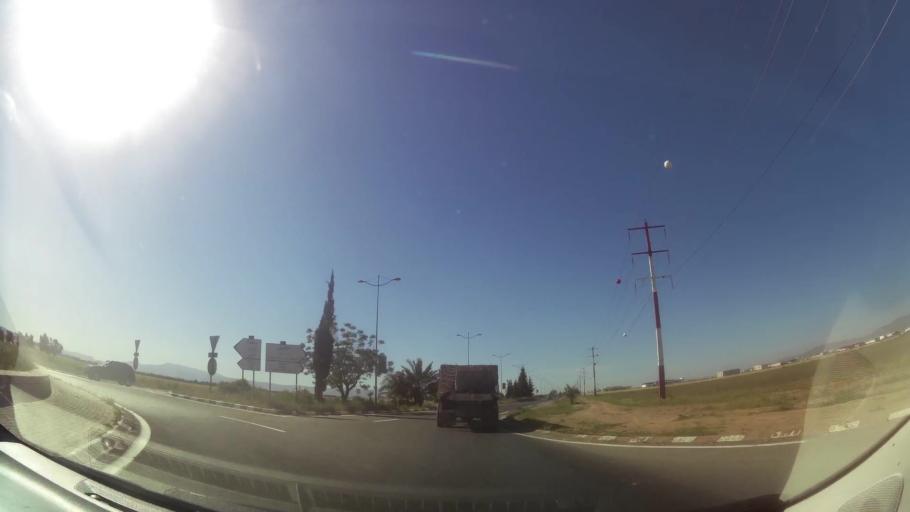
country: MA
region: Oriental
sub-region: Oujda-Angad
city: Oujda
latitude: 34.7590
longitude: -1.9370
